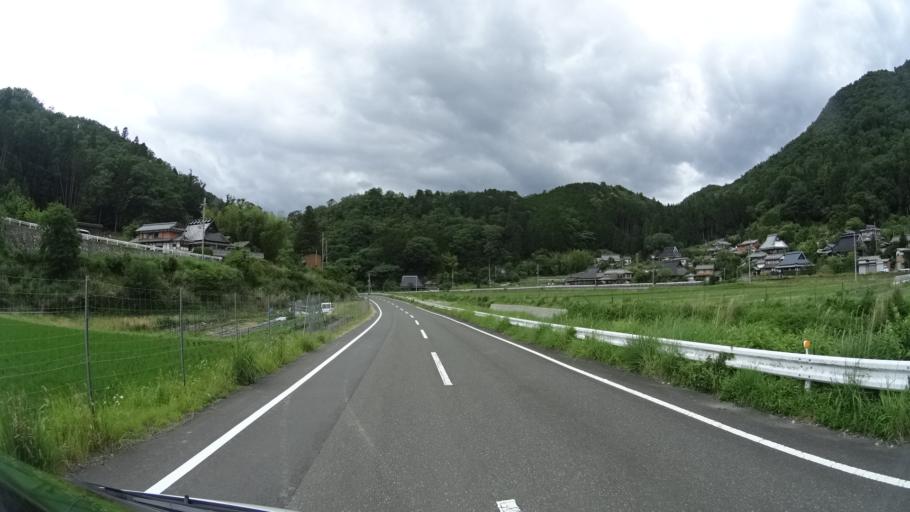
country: JP
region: Kyoto
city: Kameoka
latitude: 35.0519
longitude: 135.4091
